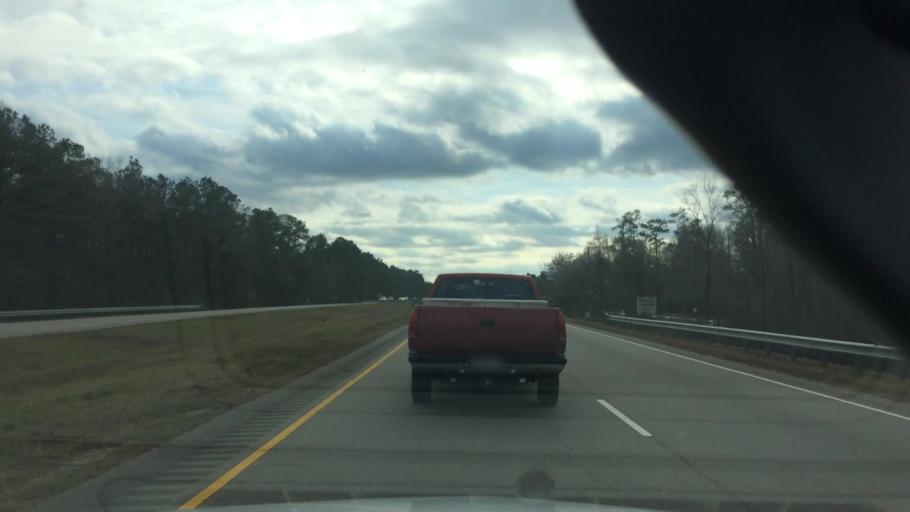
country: US
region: North Carolina
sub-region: Brunswick County
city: Bolivia
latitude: 34.1592
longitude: -78.0914
